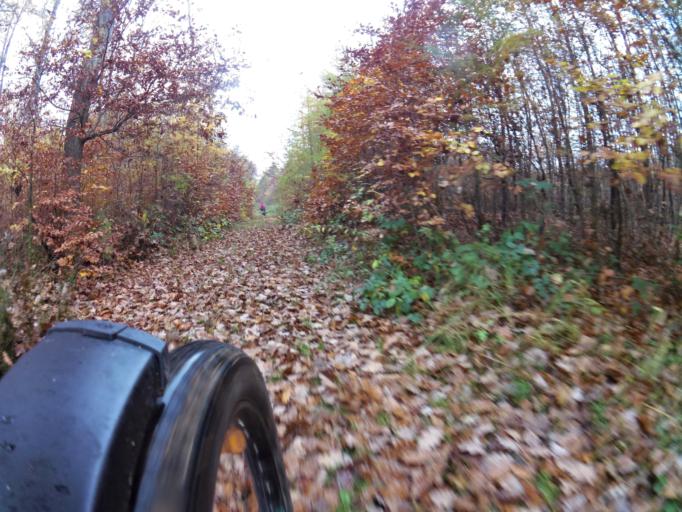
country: PL
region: Pomeranian Voivodeship
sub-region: Powiat pucki
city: Krokowa
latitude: 54.7324
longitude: 18.1316
